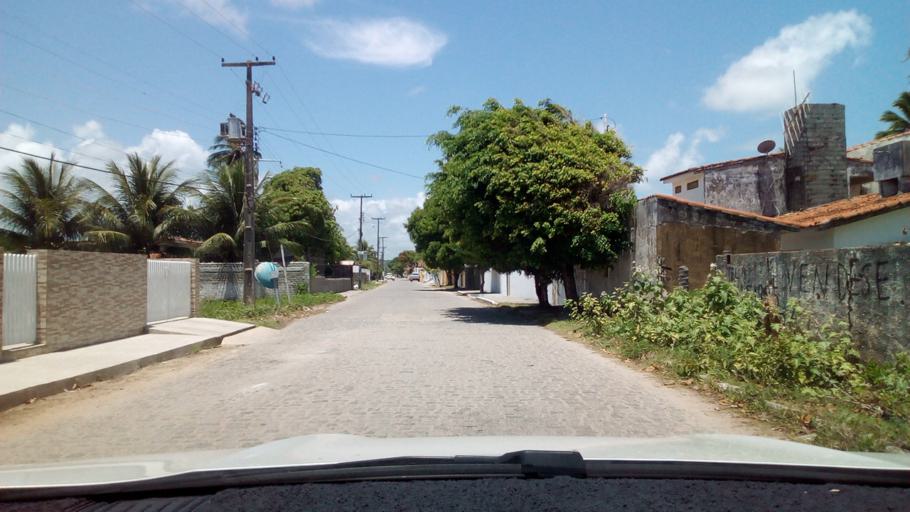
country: BR
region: Paraiba
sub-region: Pitimbu
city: Pitimbu
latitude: -7.5092
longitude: -34.8098
